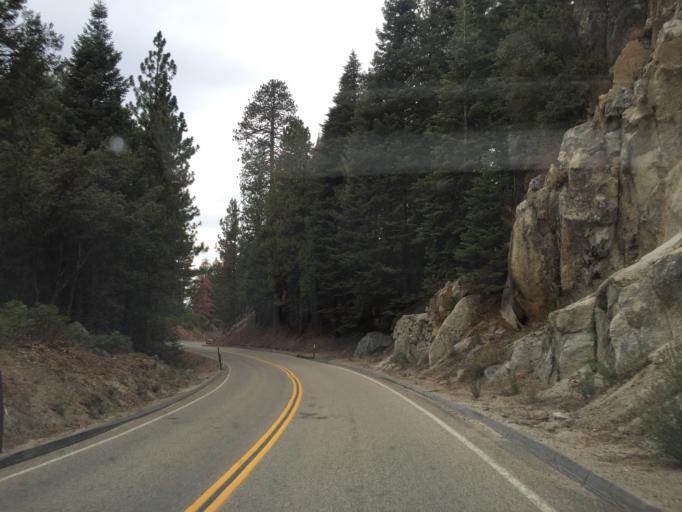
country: US
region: California
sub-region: Tulare County
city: Three Rivers
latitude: 36.7182
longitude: -118.9528
